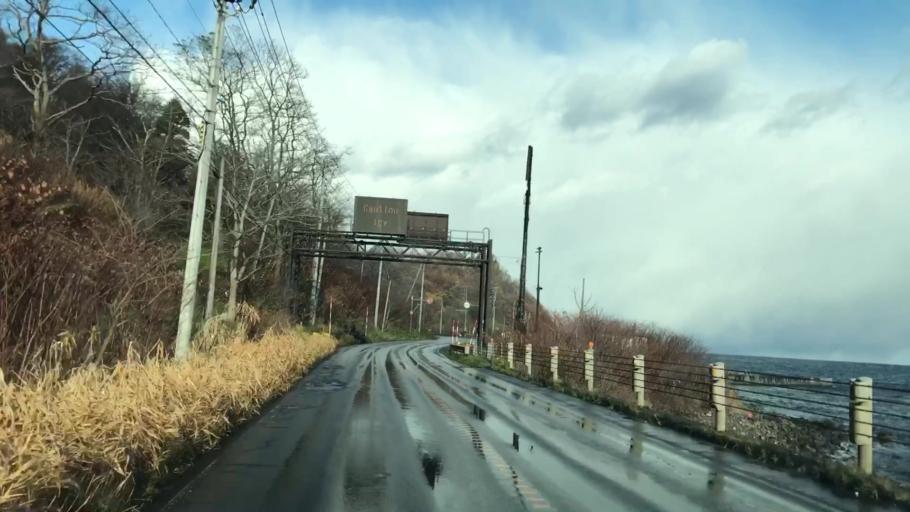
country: JP
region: Hokkaido
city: Yoichi
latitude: 43.2900
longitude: 140.6324
